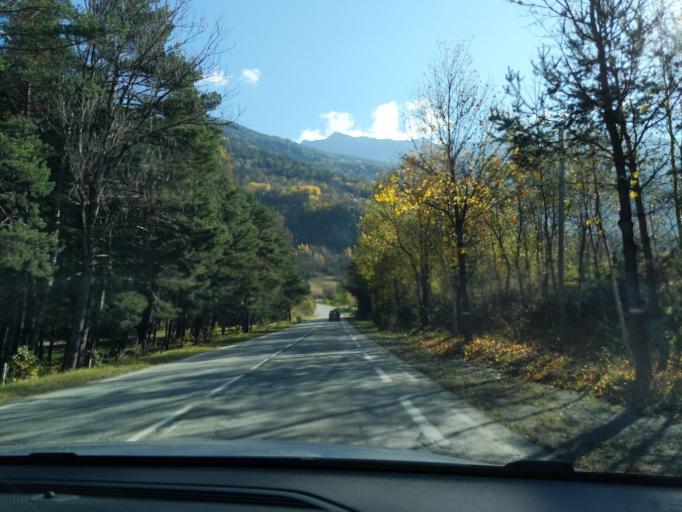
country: FR
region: Rhone-Alpes
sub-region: Departement de la Savoie
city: Seez
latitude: 45.5984
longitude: 6.8740
